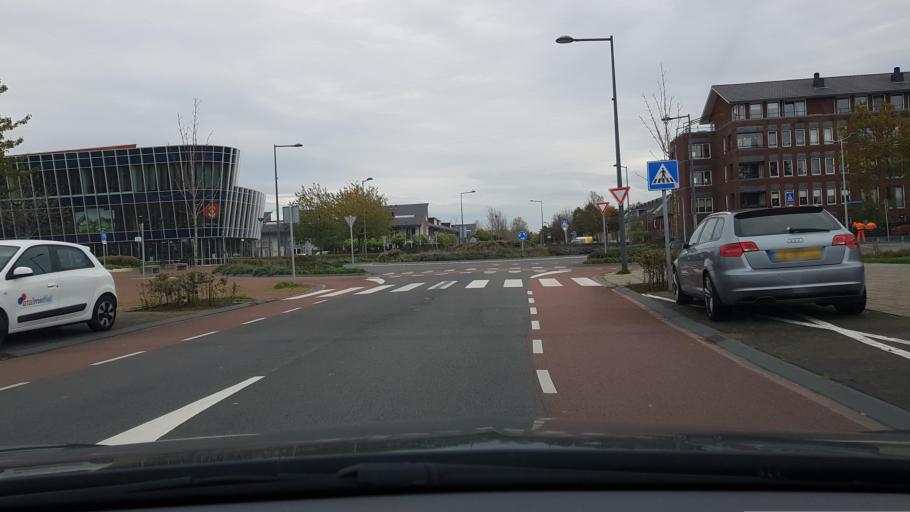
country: NL
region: North Holland
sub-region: Gemeente Haarlemmermeer
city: Hoofddorp
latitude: 52.3058
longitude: 4.6432
